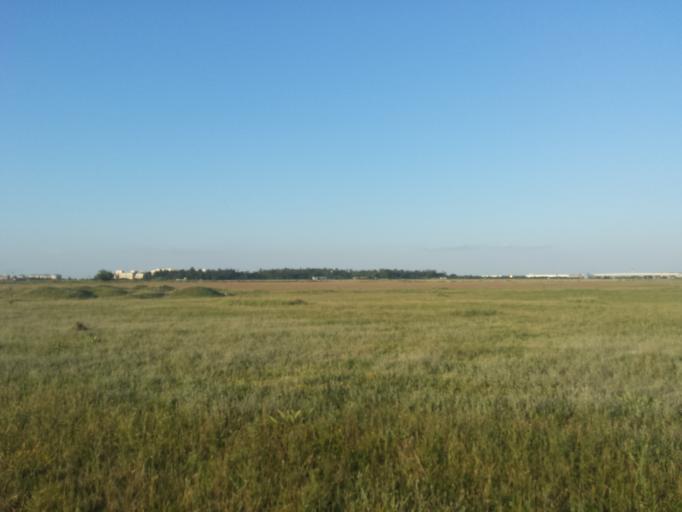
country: RO
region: Ilfov
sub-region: Comuna Tunari
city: Tunari
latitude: 44.5216
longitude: 26.1525
